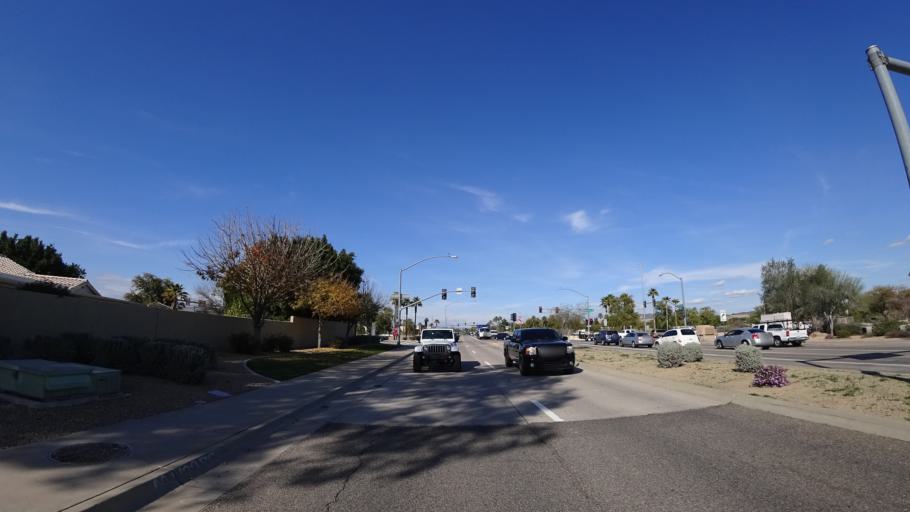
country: US
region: Arizona
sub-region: Maricopa County
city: Sun City
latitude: 33.6667
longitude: -112.2205
